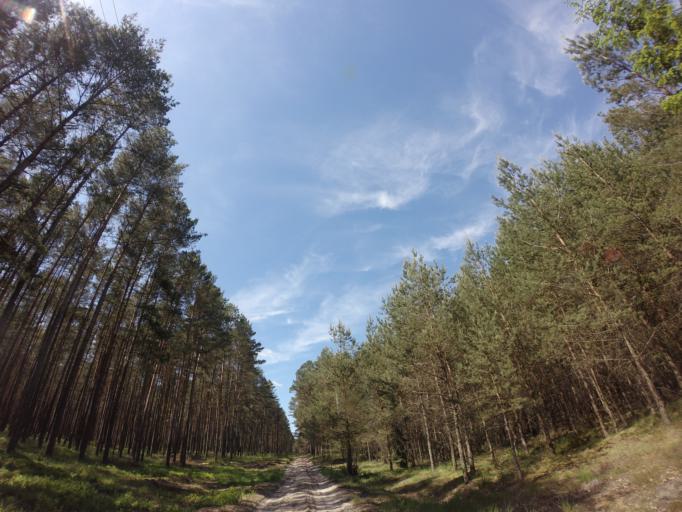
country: PL
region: West Pomeranian Voivodeship
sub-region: Powiat choszczenski
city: Drawno
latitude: 53.1252
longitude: 15.7971
